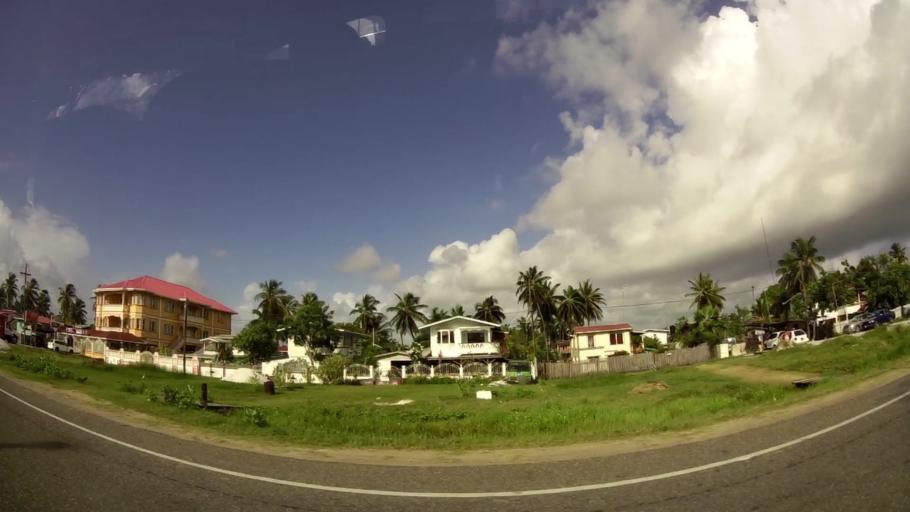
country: GY
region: Demerara-Mahaica
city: Mahaica Village
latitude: 6.7662
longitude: -57.9908
